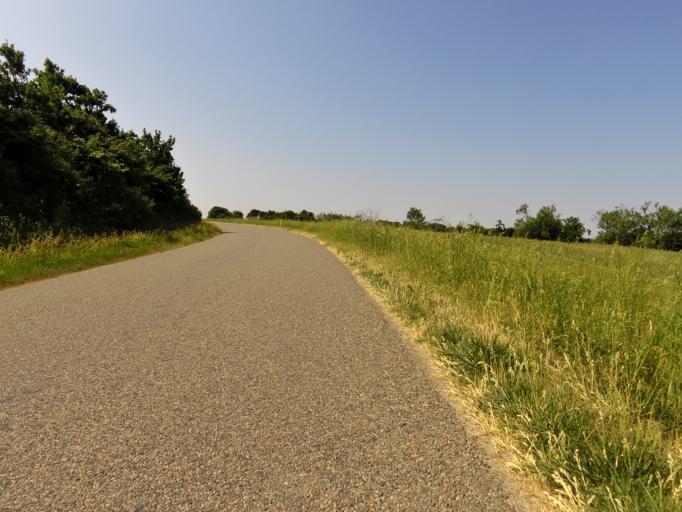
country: DK
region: Central Jutland
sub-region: Holstebro Kommune
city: Vinderup
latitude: 56.4761
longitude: 8.8193
